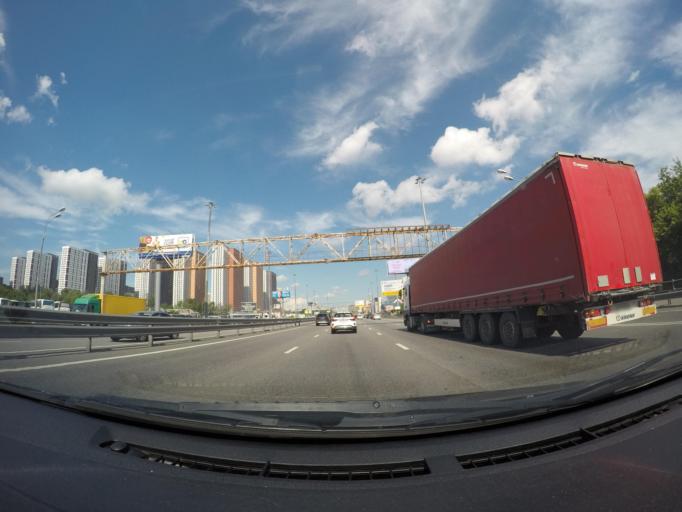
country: RU
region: Moskovskaya
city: Lyubertsy
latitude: 55.6722
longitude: 37.8650
